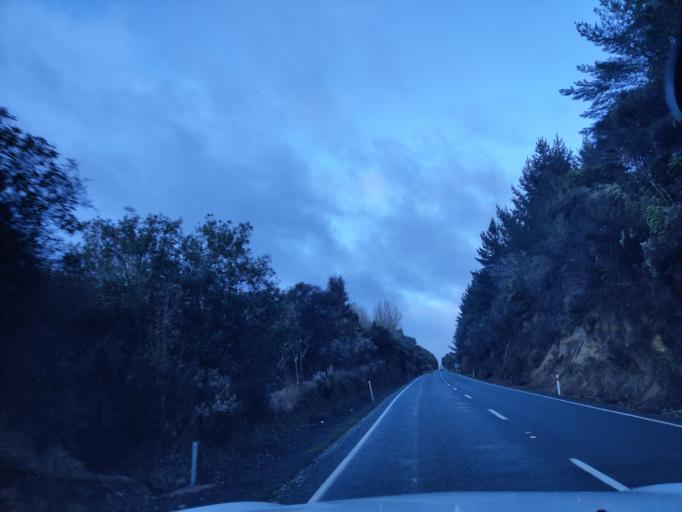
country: NZ
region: Waikato
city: Turangi
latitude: -38.7021
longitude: 175.6804
